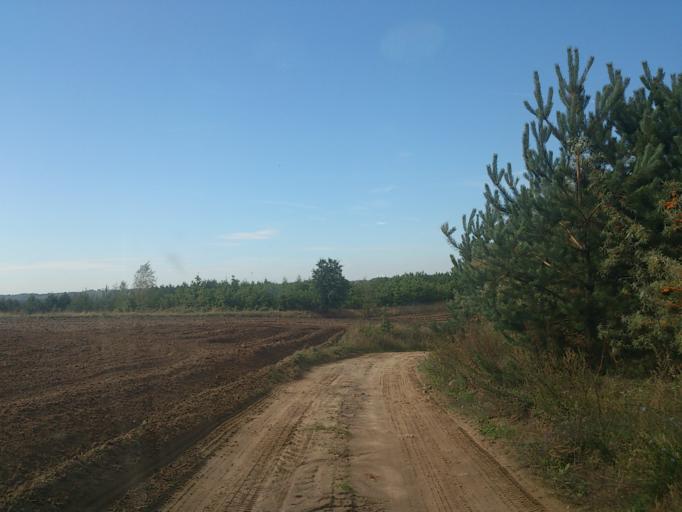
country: PL
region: Kujawsko-Pomorskie
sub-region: Powiat golubsko-dobrzynski
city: Radomin
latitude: 53.1215
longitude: 19.1322
